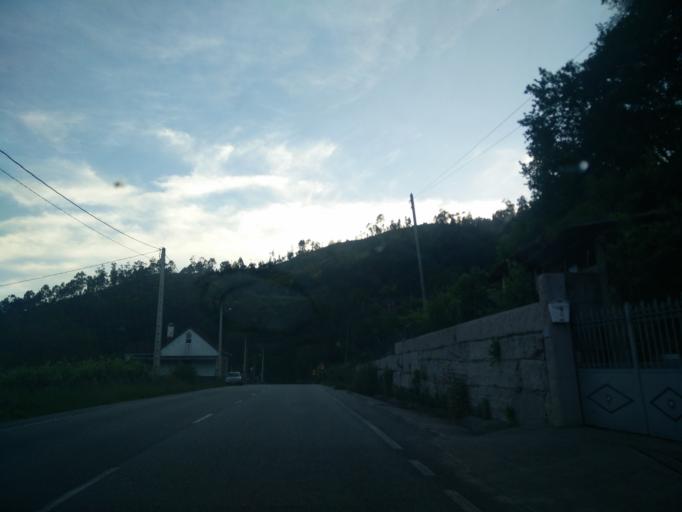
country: ES
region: Galicia
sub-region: Provincia de Pontevedra
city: Mondariz
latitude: 42.2429
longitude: -8.4500
